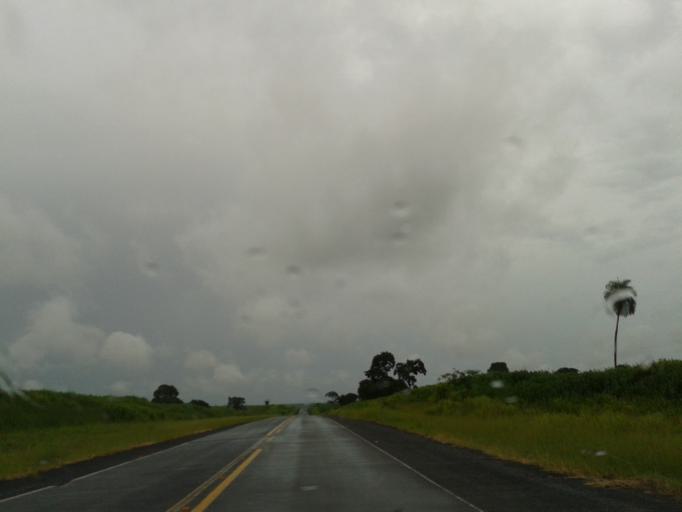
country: BR
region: Minas Gerais
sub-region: Santa Vitoria
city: Santa Vitoria
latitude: -19.1557
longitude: -50.1288
